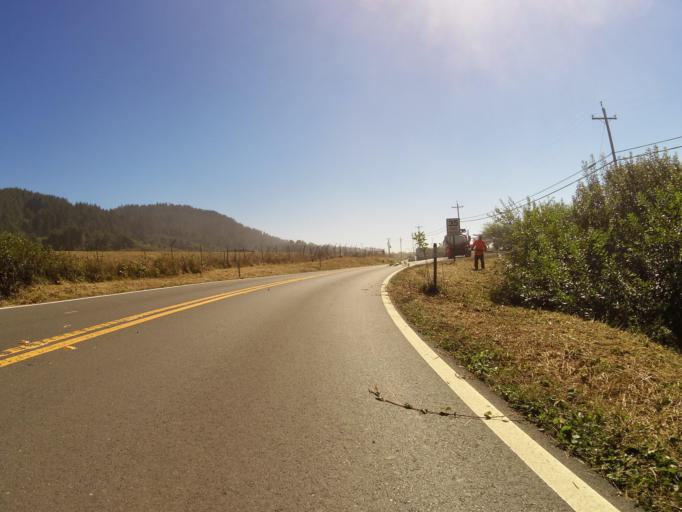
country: US
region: California
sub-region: Mendocino County
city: Fort Bragg
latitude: 39.6441
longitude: -123.7840
